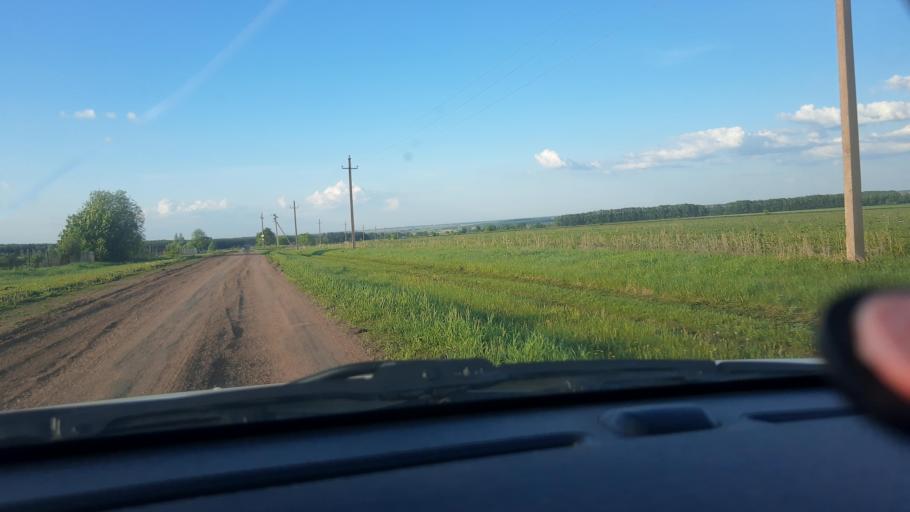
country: RU
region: Bashkortostan
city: Karmaskaly
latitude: 54.3900
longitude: 55.9450
